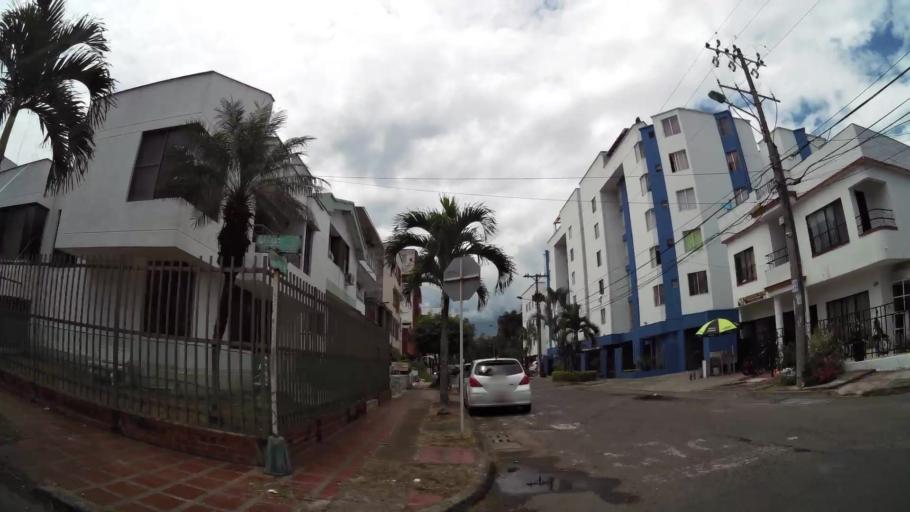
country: CO
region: Valle del Cauca
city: Cali
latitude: 3.3851
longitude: -76.5277
